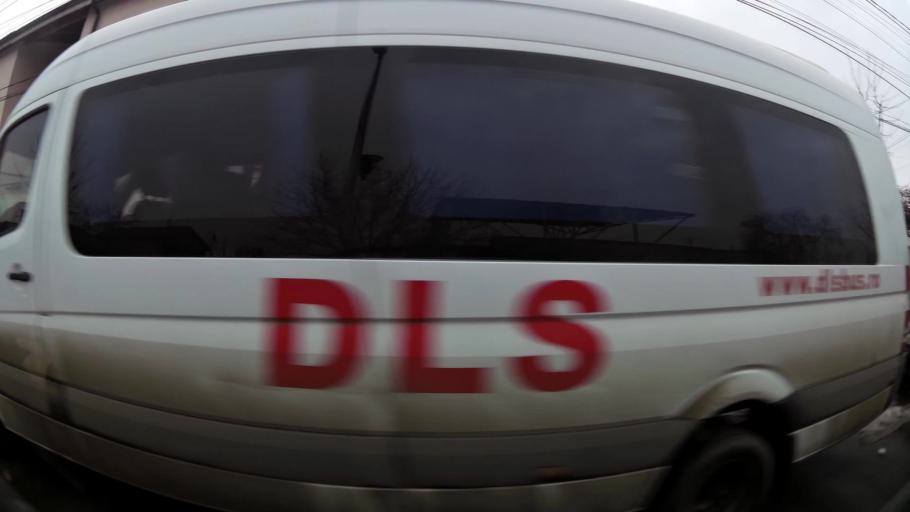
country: RO
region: Ilfov
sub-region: Voluntari City
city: Voluntari
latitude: 44.4814
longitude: 26.1717
